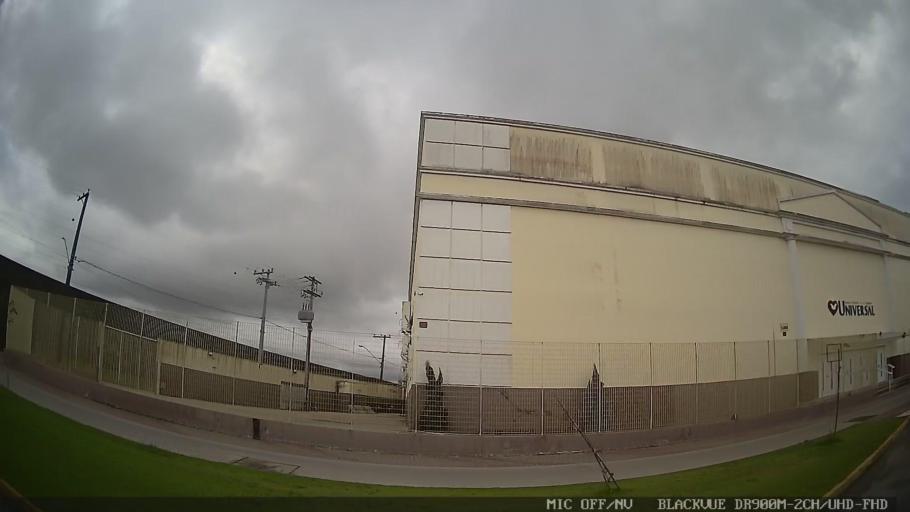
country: BR
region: Sao Paulo
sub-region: Itanhaem
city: Itanhaem
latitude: -24.1749
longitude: -46.7796
